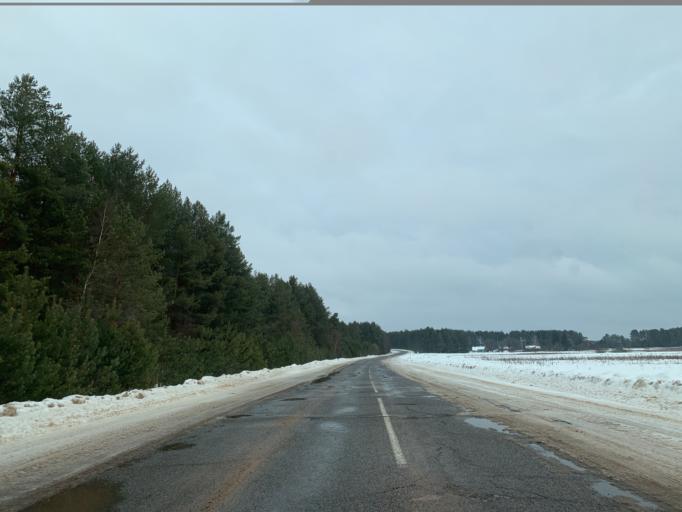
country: BY
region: Minsk
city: Il'ya
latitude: 54.3250
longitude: 27.2482
